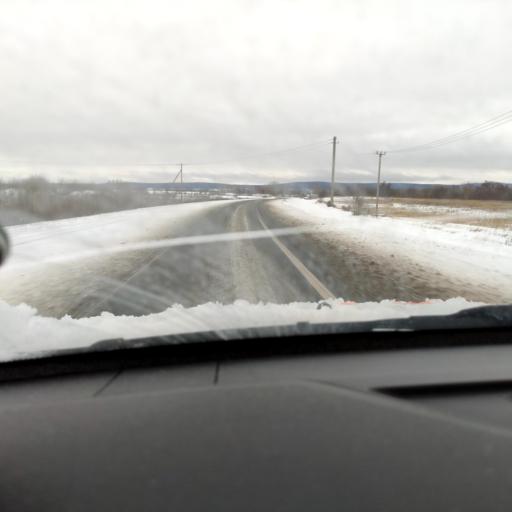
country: RU
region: Samara
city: Novosemeykino
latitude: 53.4193
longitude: 50.3496
